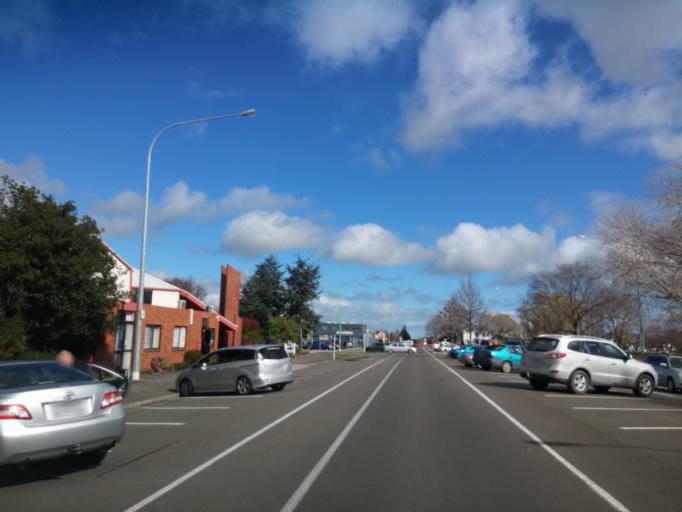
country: NZ
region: Manawatu-Wanganui
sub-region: Palmerston North City
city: Palmerston North
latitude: -40.3601
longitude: 175.6058
